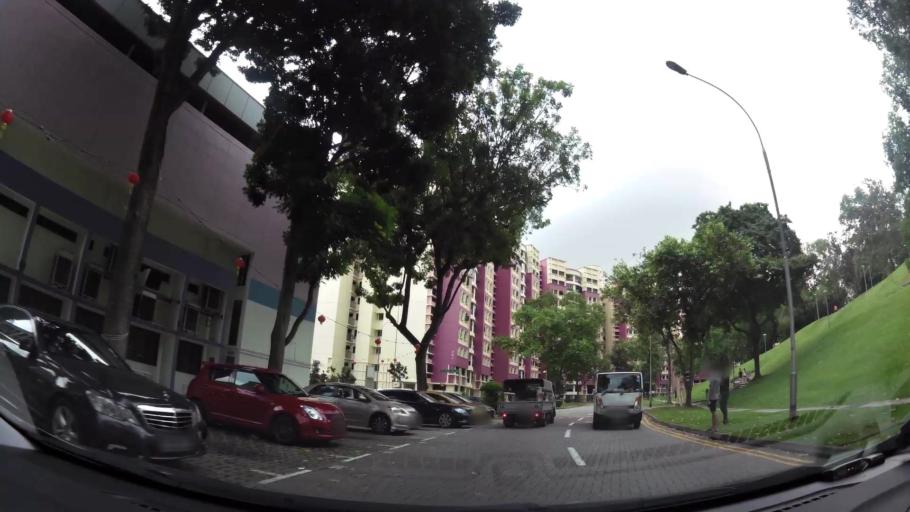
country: MY
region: Johor
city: Kampung Pasir Gudang Baru
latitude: 1.4364
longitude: 103.8361
